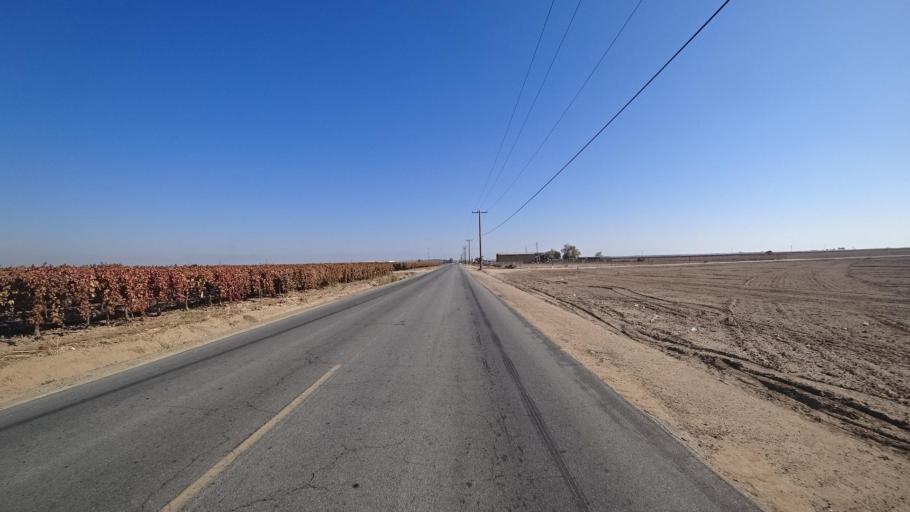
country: US
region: California
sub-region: Kern County
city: McFarland
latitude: 35.7179
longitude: -119.1658
